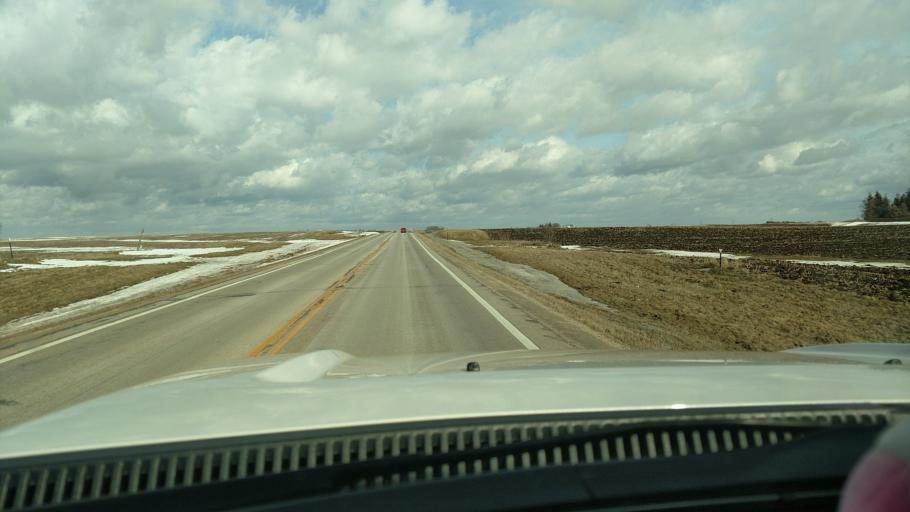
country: US
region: Minnesota
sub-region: Wabasha County
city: Plainview
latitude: 44.2071
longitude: -92.1094
